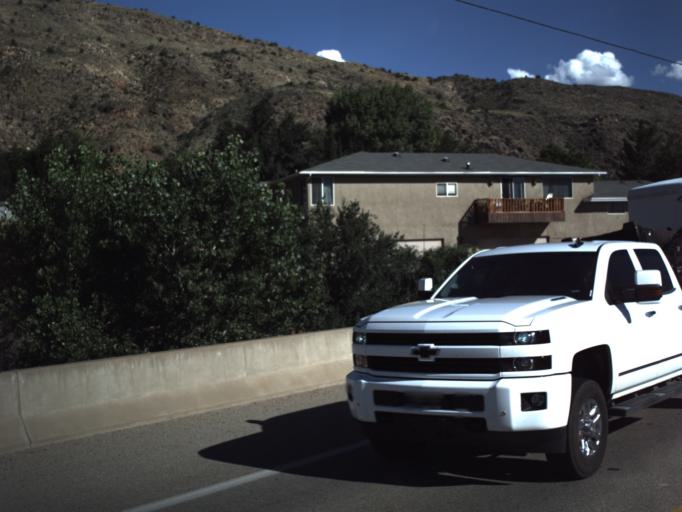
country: US
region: Utah
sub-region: Washington County
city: Toquerville
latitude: 37.2575
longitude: -113.2859
